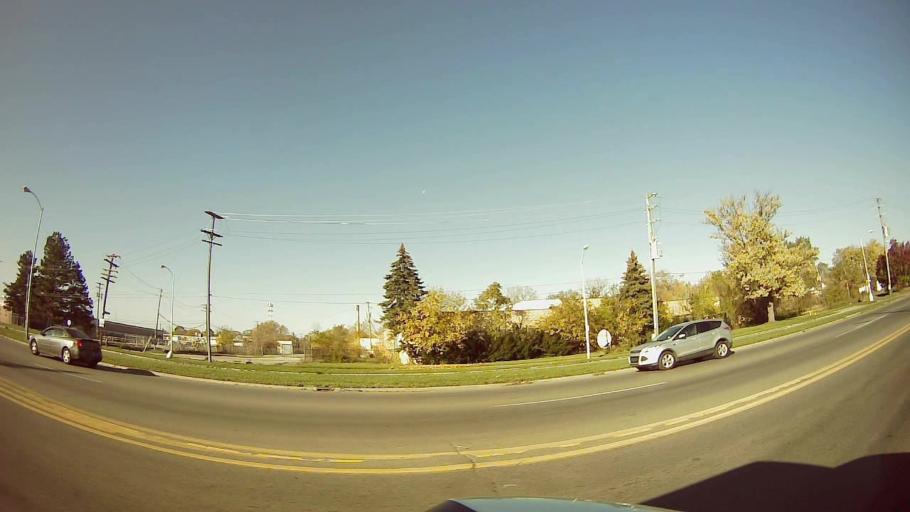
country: US
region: Michigan
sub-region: Wayne County
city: Dearborn
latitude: 42.3828
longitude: -83.1979
